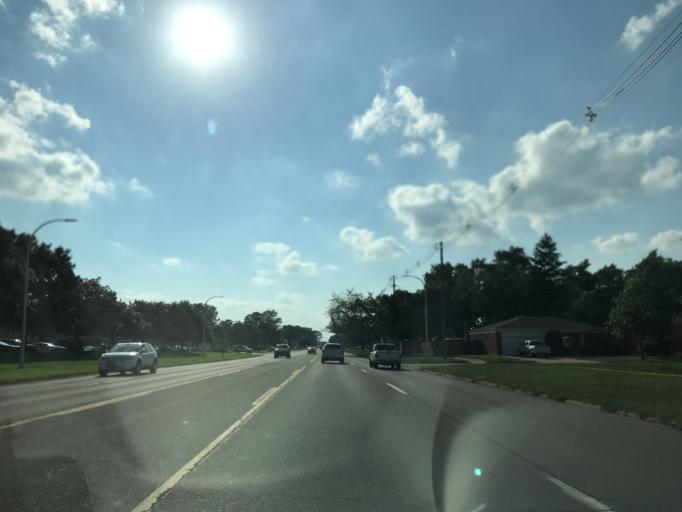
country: US
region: Michigan
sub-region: Wayne County
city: Livonia
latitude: 42.3978
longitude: -83.3476
